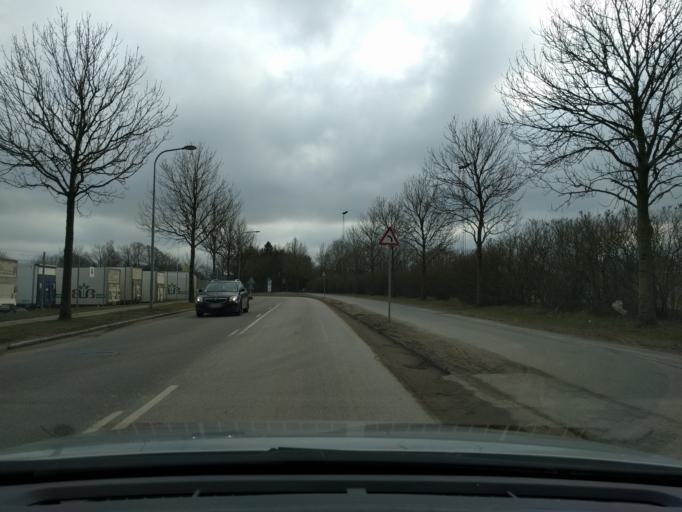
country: DK
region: South Denmark
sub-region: Odense Kommune
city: Bellinge
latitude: 55.3602
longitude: 10.3238
